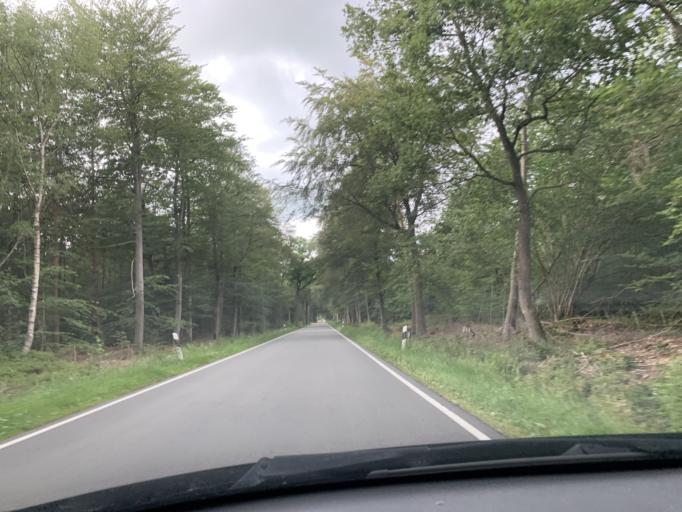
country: DE
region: Lower Saxony
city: Westerstede
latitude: 53.2180
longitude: 7.9145
